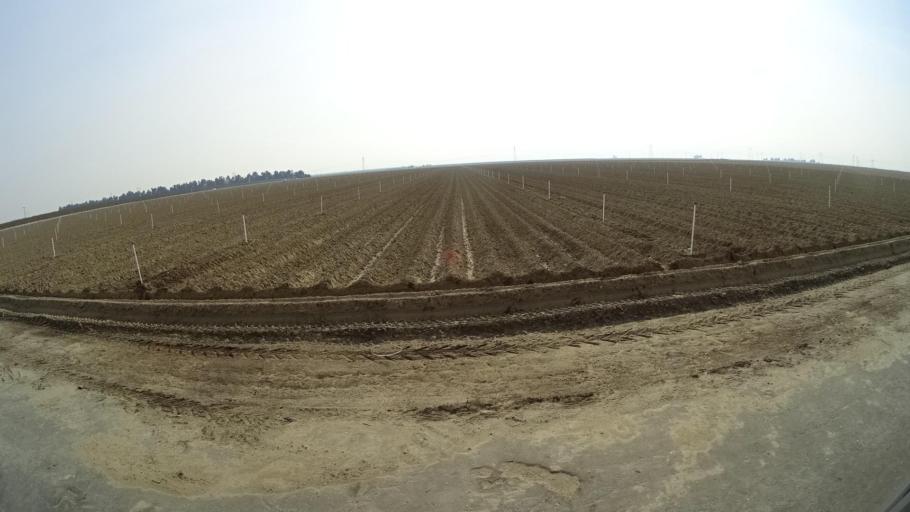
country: US
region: California
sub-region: Kern County
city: Weedpatch
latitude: 35.1367
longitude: -118.9709
